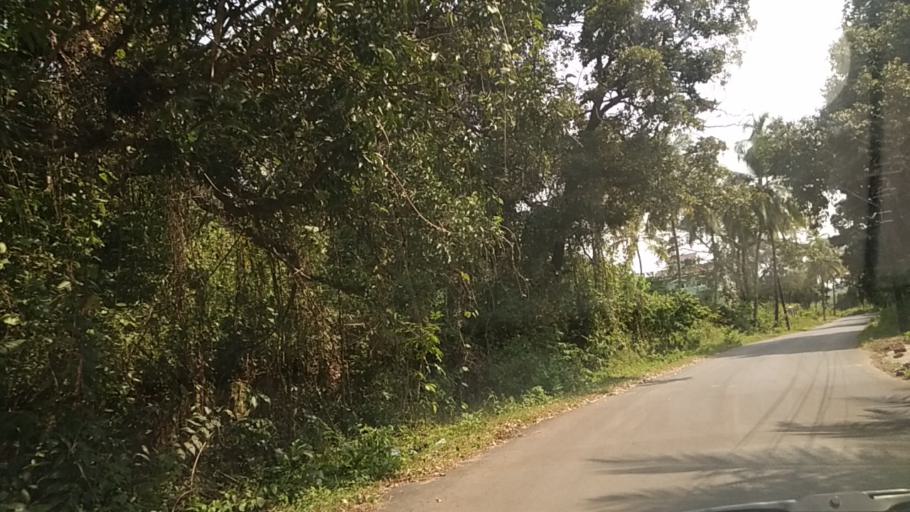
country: IN
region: Goa
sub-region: North Goa
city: Bambolim
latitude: 15.4420
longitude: 73.8618
